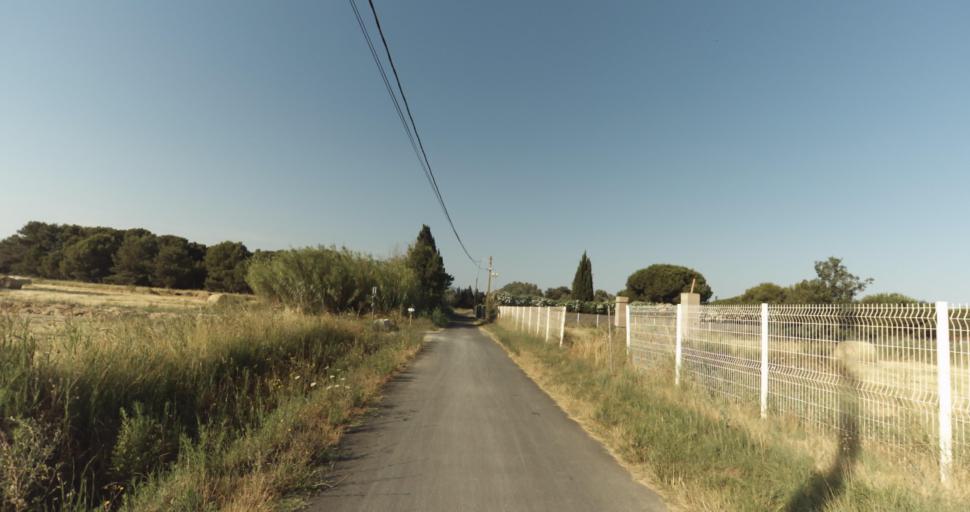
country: FR
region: Languedoc-Roussillon
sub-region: Departement des Pyrenees-Orientales
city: Alenya
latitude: 42.6387
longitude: 3.0074
